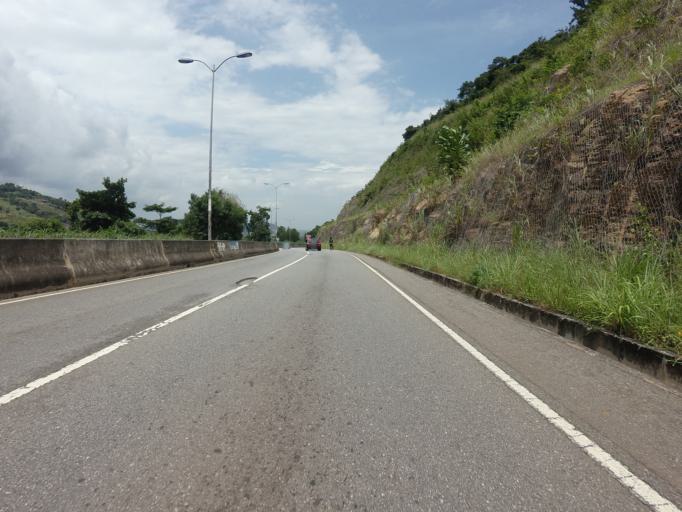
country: GH
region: Eastern
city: Aburi
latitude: 5.7885
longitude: -0.1872
